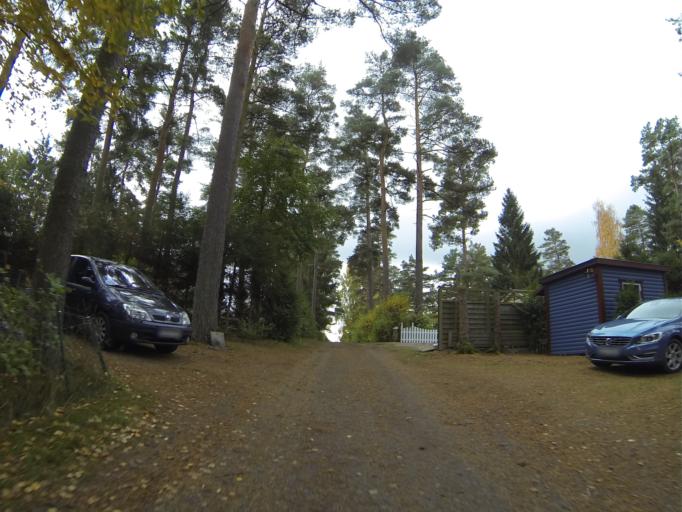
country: SE
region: Skane
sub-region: Sjobo Kommun
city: Sjoebo
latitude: 55.6324
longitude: 13.6635
